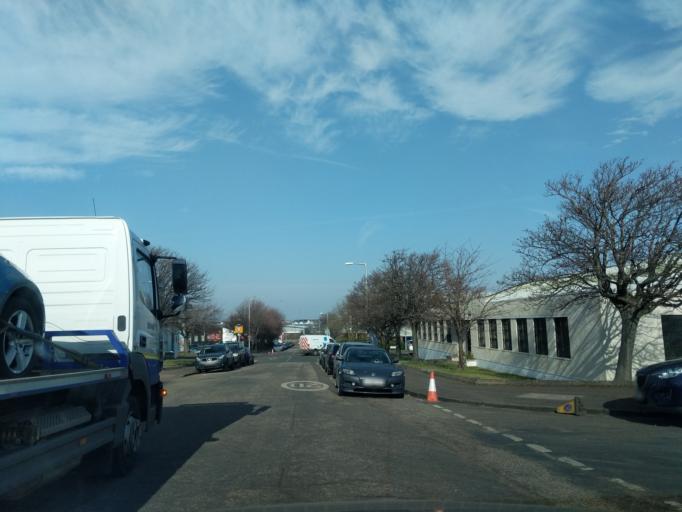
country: GB
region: Scotland
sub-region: Edinburgh
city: Currie
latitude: 55.9258
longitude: -3.2979
